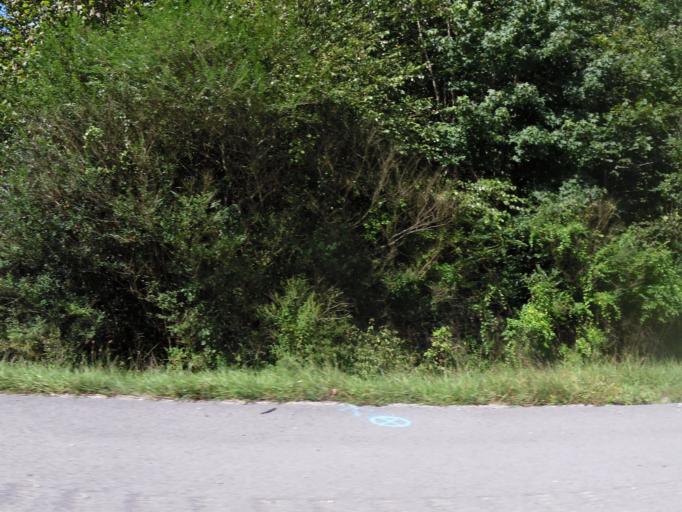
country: US
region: Kentucky
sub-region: Bell County
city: Pineville
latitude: 36.7821
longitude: -83.5727
